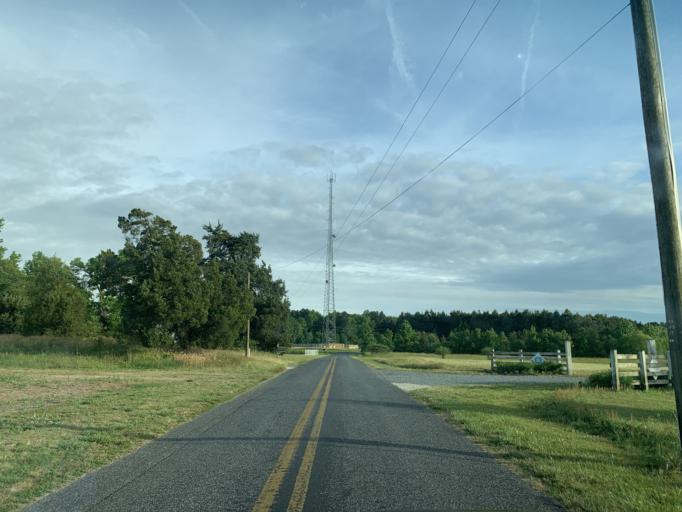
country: US
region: Maryland
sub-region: Worcester County
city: Pocomoke City
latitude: 38.0909
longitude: -75.4642
